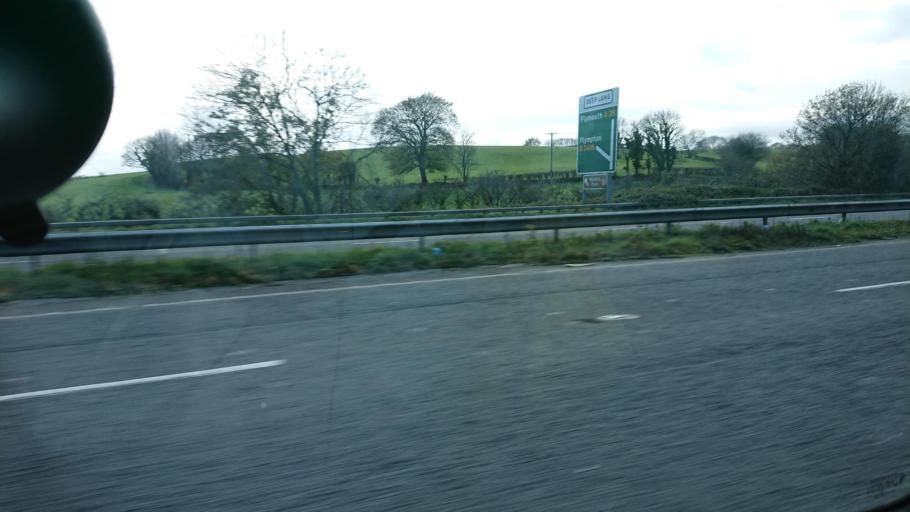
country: GB
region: England
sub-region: Devon
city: Yealmpton
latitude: 50.3798
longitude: -4.0179
